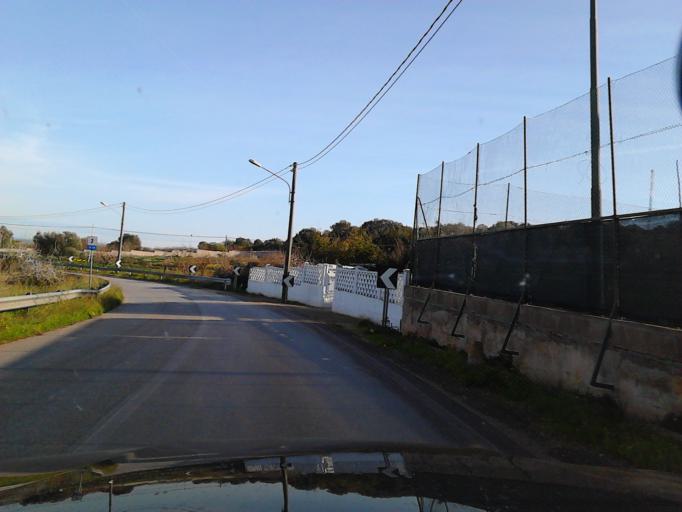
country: IT
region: Apulia
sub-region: Provincia di Bari
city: Mola di Bari
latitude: 41.0386
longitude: 17.0521
